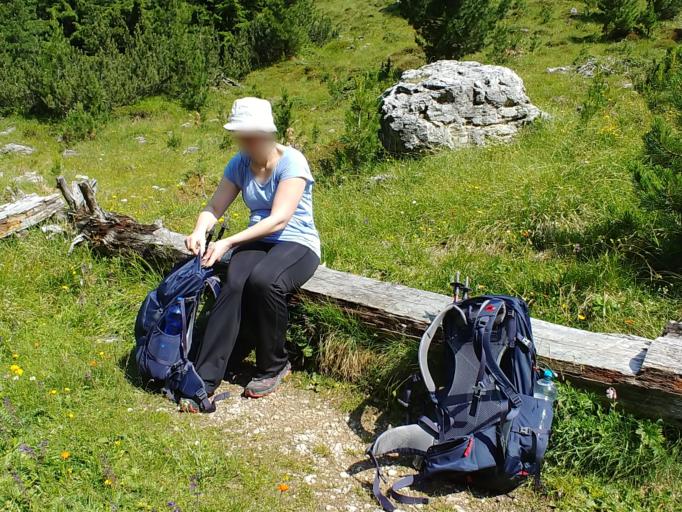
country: IT
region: Trentino-Alto Adige
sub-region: Bolzano
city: Selva
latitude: 46.5621
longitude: 11.7990
